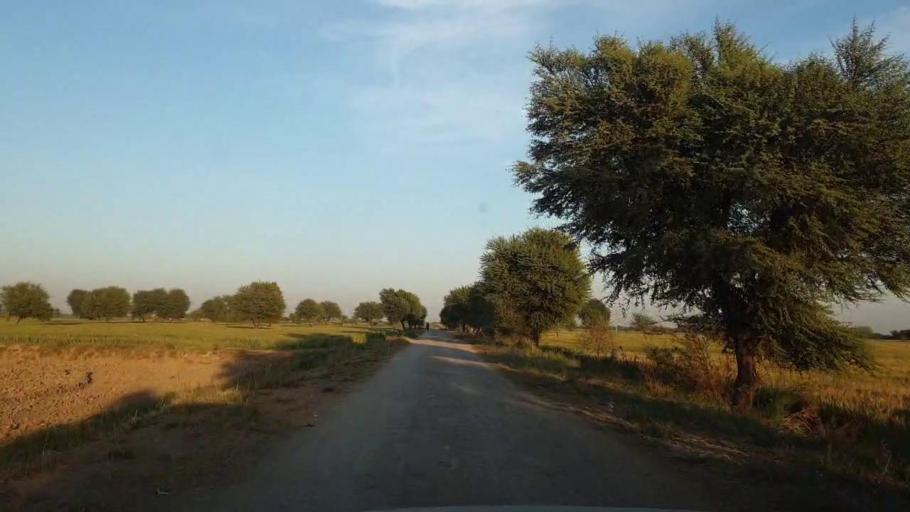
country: PK
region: Sindh
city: Kunri
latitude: 25.1288
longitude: 69.4390
